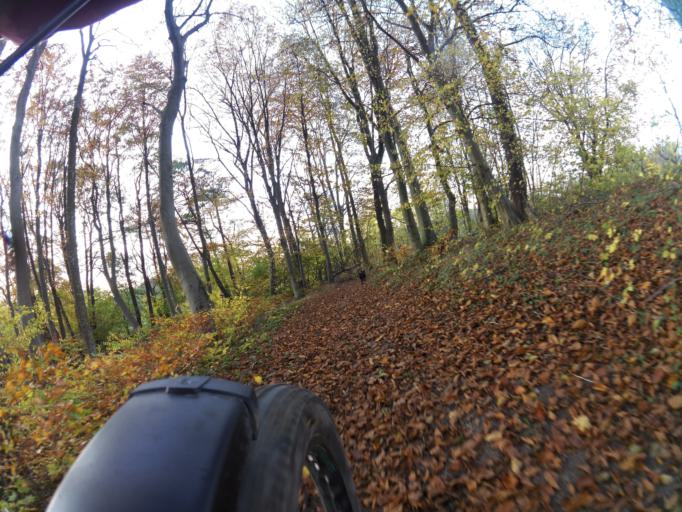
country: PL
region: Pomeranian Voivodeship
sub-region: Powiat pucki
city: Krokowa
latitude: 54.7723
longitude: 18.1710
